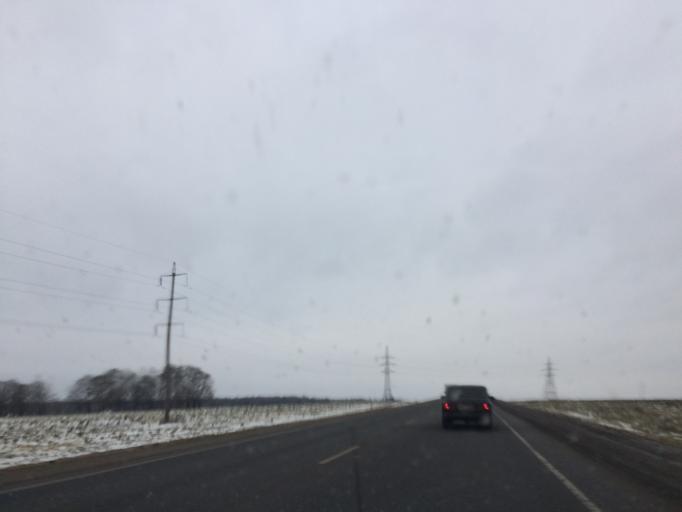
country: RU
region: Tula
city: Kosaya Gora
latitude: 54.1578
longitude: 37.5218
